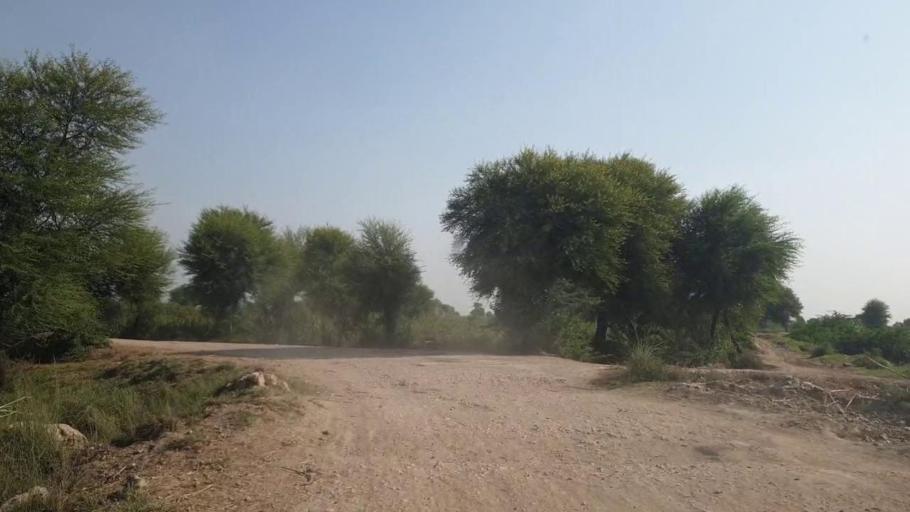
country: PK
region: Sindh
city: Sinjhoro
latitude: 26.0556
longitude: 68.8318
